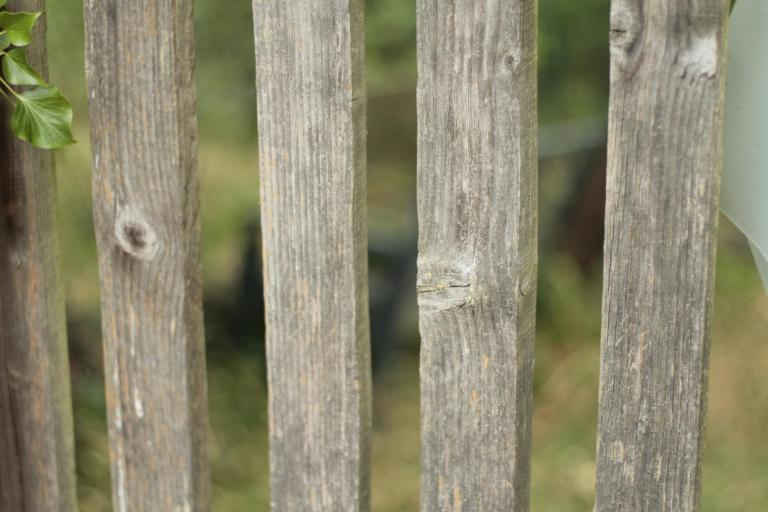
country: DE
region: Hesse
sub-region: Regierungsbezirk Darmstadt
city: Bensheim
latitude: 49.6868
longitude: 8.6294
